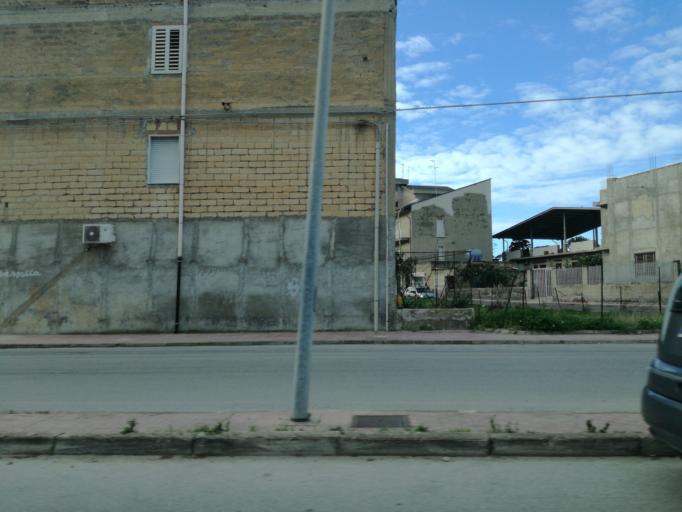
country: IT
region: Sicily
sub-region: Provincia di Caltanissetta
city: Gela
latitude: 37.0759
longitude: 14.2206
